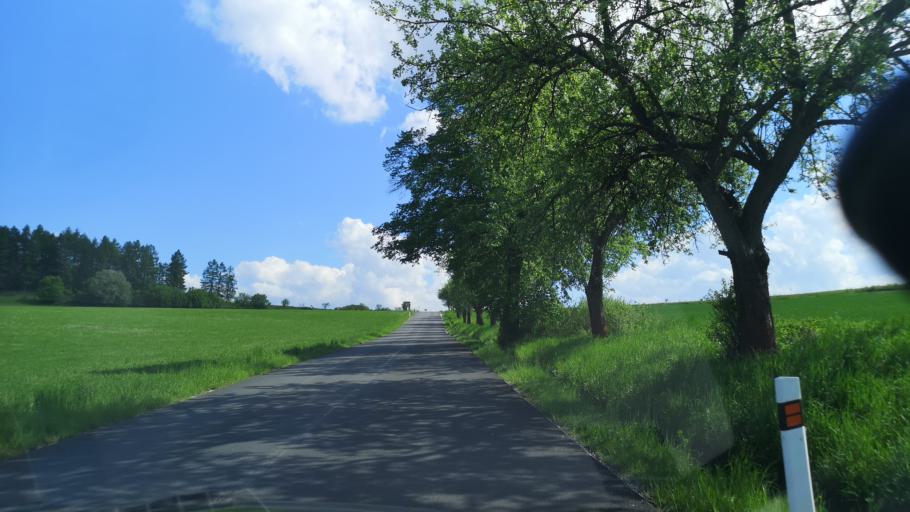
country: SK
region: Presovsky
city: Spisske Podhradie
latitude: 49.0010
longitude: 20.7779
